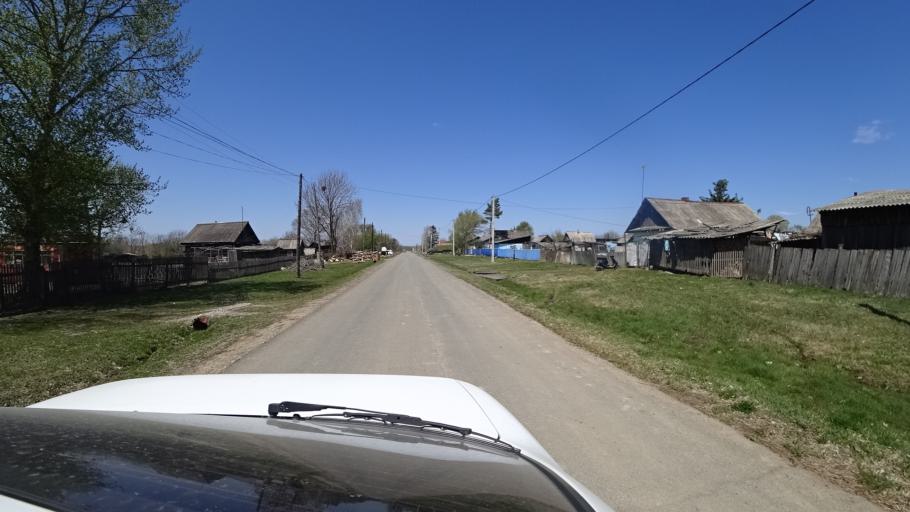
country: RU
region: Primorskiy
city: Dal'nerechensk
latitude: 45.7933
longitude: 133.7721
